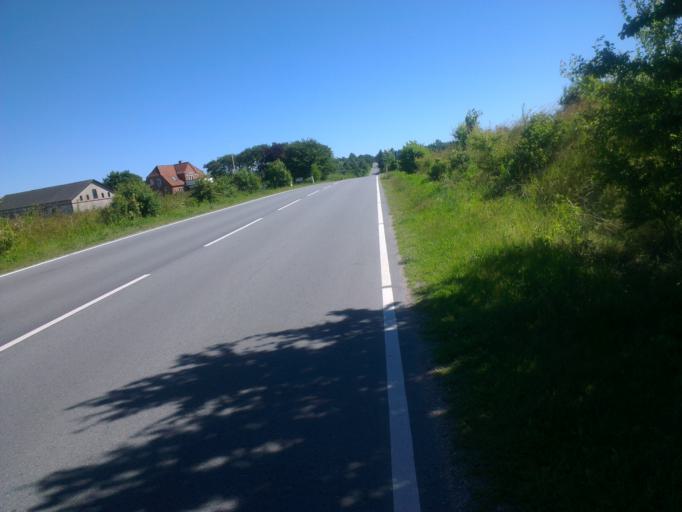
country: DK
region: Capital Region
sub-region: Halsnaes Kommune
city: Hundested
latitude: 55.9339
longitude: 11.9099
